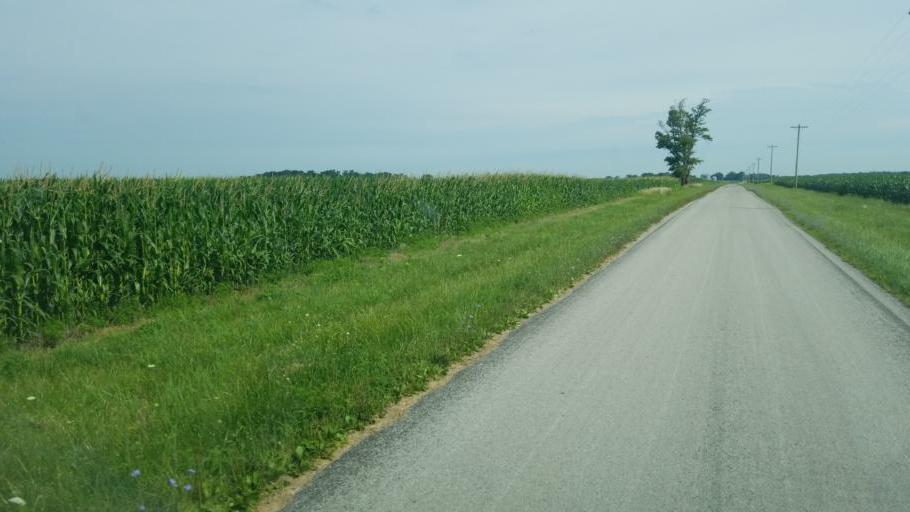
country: US
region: Ohio
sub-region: Wyandot County
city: Upper Sandusky
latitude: 40.7531
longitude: -83.3240
